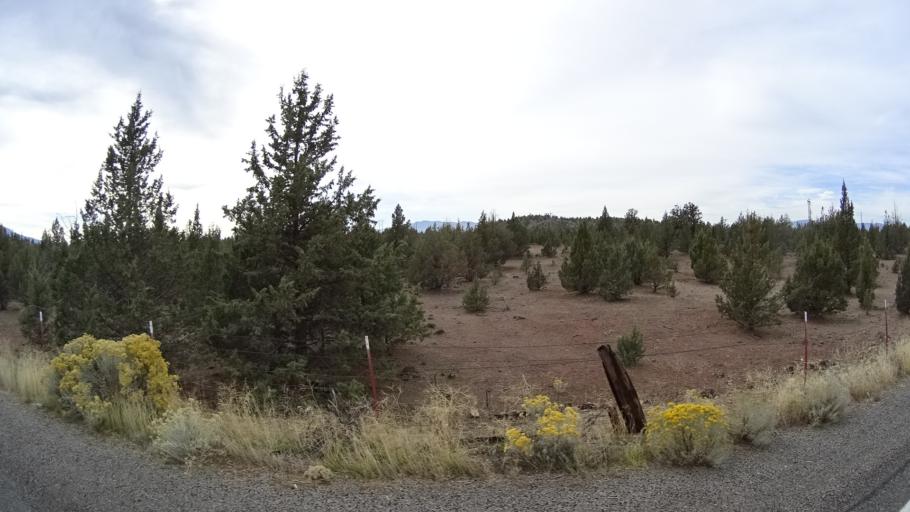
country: US
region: California
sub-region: Siskiyou County
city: Weed
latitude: 41.6068
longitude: -122.3618
